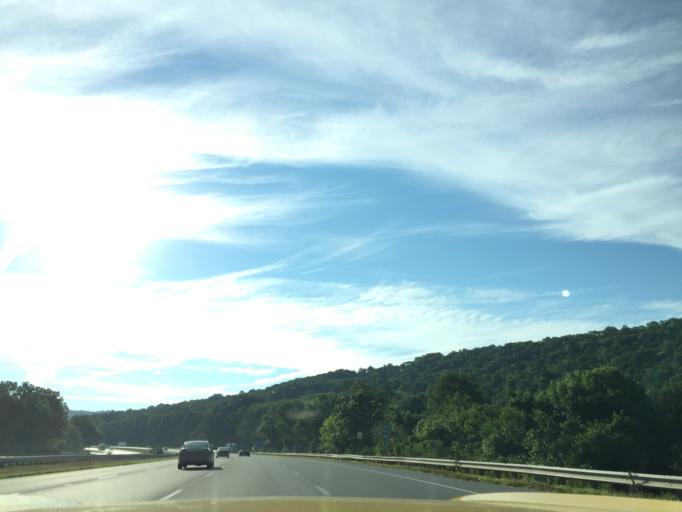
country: US
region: New Jersey
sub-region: Warren County
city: Alpha
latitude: 40.6591
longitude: -75.0657
